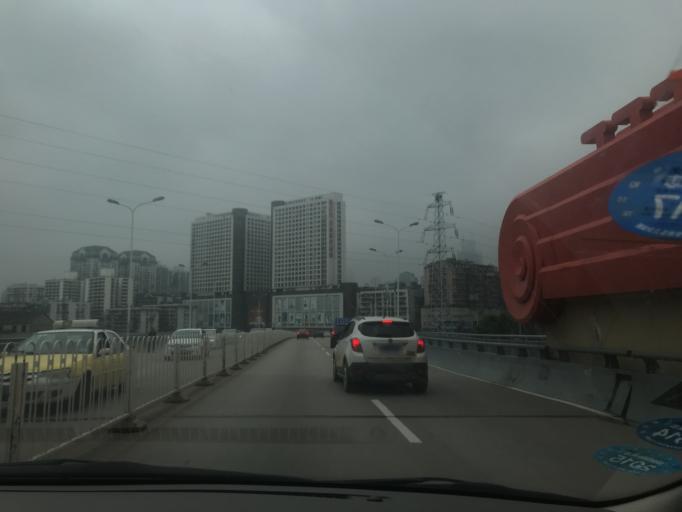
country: CN
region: Hubei
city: Wuhan
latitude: 30.5668
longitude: 114.2781
